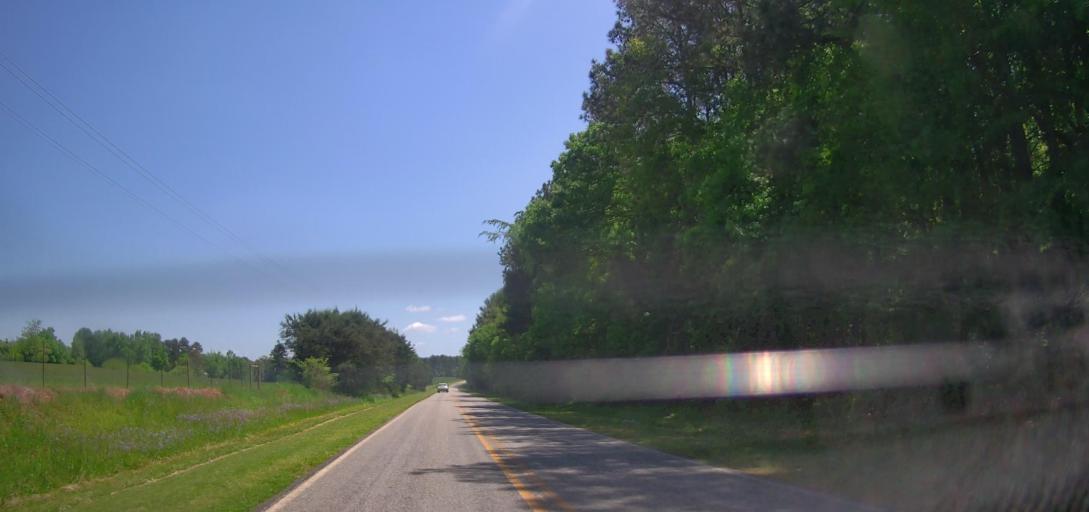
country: US
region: Georgia
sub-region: Jasper County
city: Monticello
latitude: 33.2788
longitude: -83.6692
